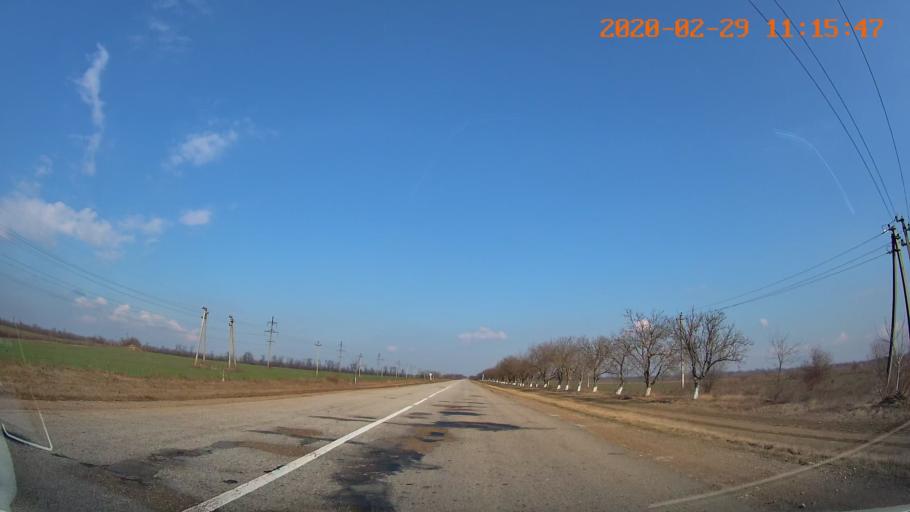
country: MD
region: Telenesti
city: Dubasari
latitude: 47.2994
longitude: 29.1660
